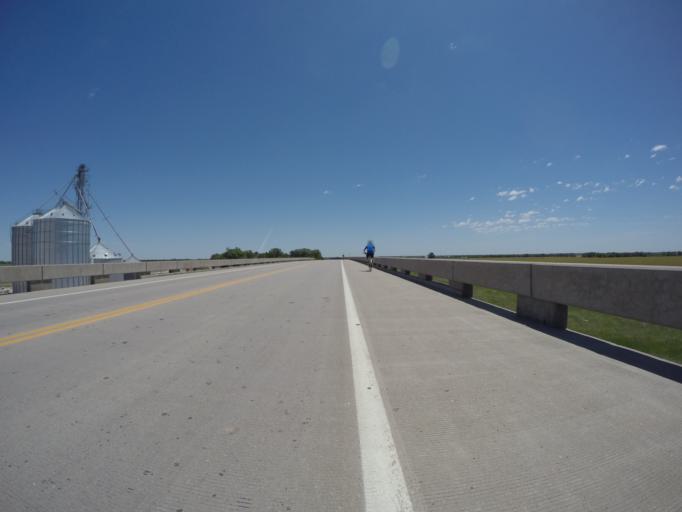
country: US
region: Kansas
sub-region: Republic County
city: Belleville
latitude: 39.8119
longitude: -97.7132
